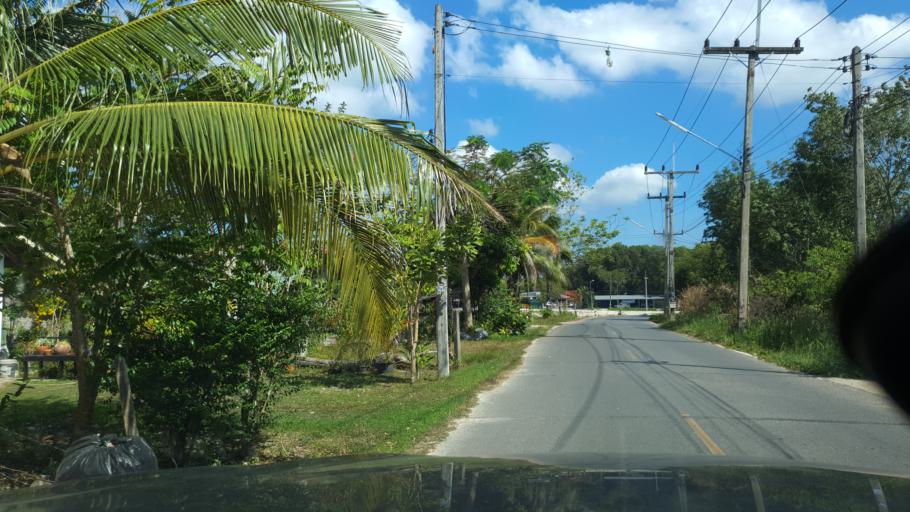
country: TH
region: Phangnga
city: Ban Ao Nang
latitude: 8.0330
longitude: 98.8572
